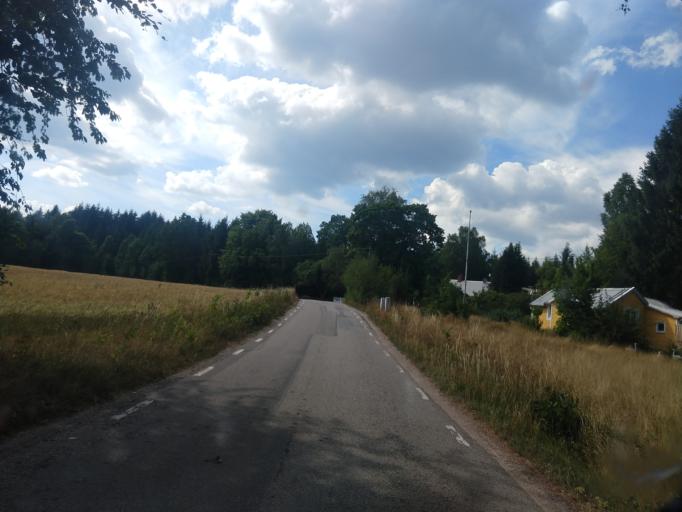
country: SE
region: Blekinge
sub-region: Karlskrona Kommun
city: Nattraby
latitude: 56.2572
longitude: 15.5225
